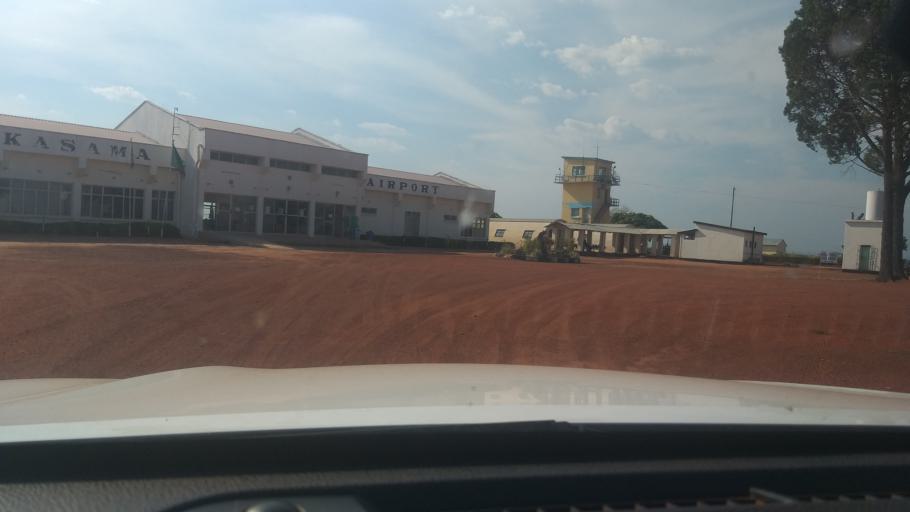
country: ZM
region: Northern
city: Kasama
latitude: -10.2177
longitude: 31.1361
